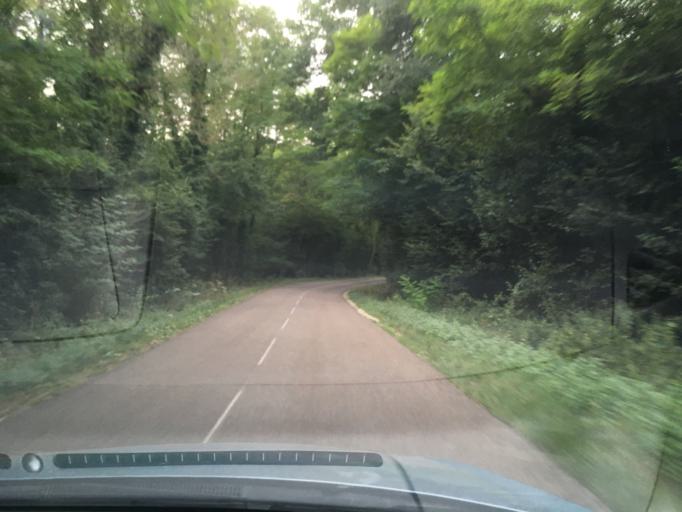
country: FR
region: Bourgogne
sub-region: Departement de l'Yonne
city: Appoigny
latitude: 47.8720
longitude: 3.4955
